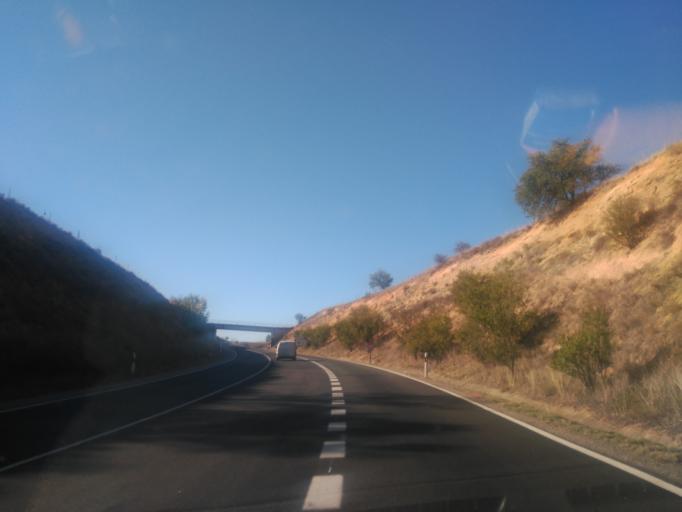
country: ES
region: Castille and Leon
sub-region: Provincia de Burgos
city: Fuentecen
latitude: 41.6319
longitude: -3.8721
